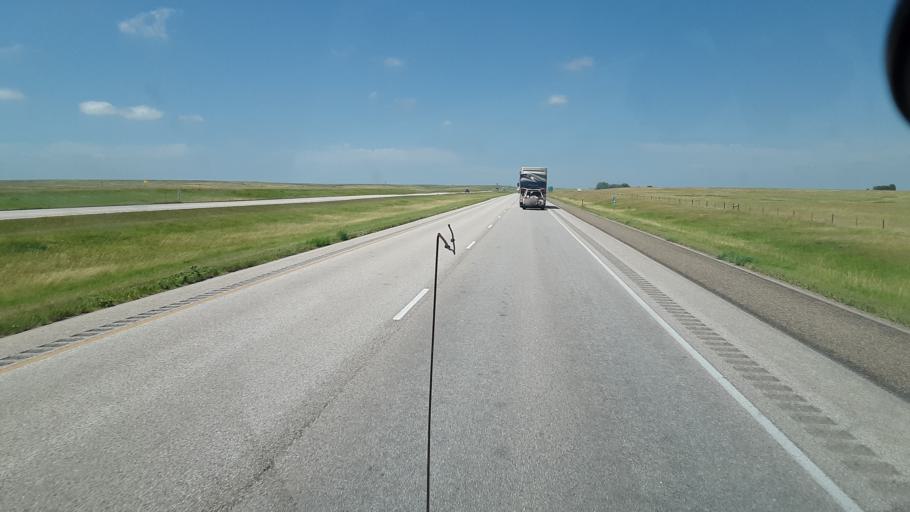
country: US
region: South Dakota
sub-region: Jackson County
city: Kadoka
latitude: 43.8363
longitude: -101.6449
